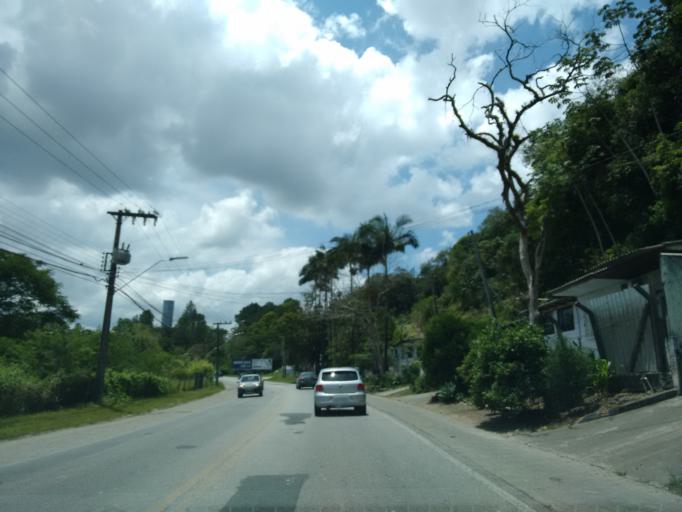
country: BR
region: Santa Catarina
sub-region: Blumenau
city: Blumenau
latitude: -26.9055
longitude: -49.0163
